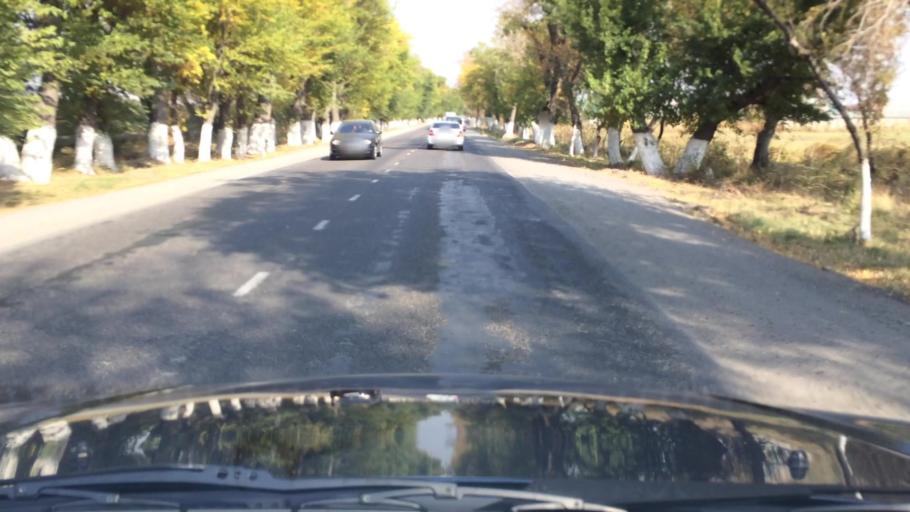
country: KG
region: Chuy
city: Lebedinovka
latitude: 42.9082
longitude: 74.6870
